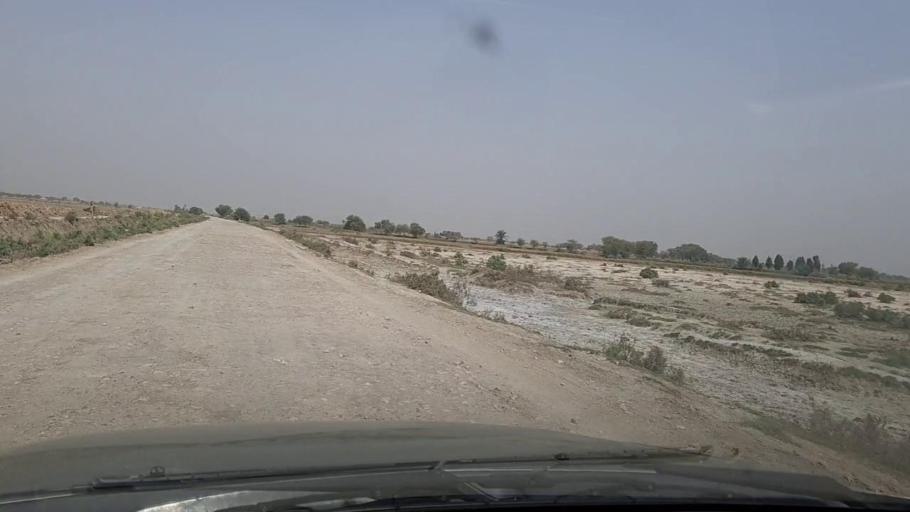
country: PK
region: Sindh
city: Thul
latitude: 28.4066
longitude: 68.7012
